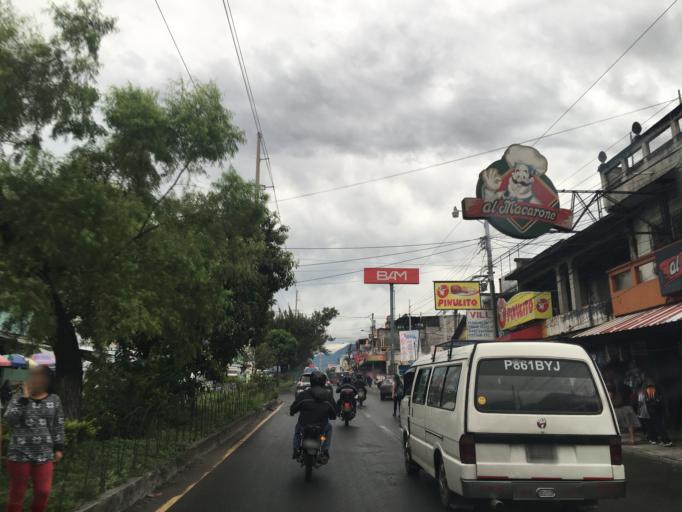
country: GT
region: Guatemala
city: Petapa
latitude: 14.5211
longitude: -90.5422
